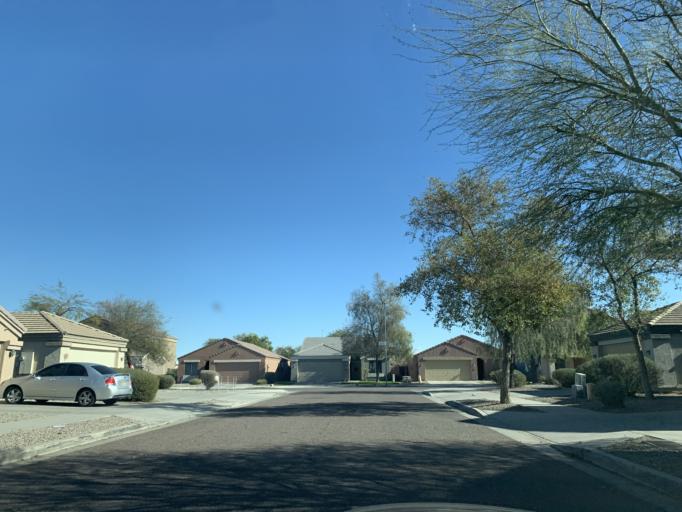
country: US
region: Arizona
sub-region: Maricopa County
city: Laveen
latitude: 33.3950
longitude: -112.1263
